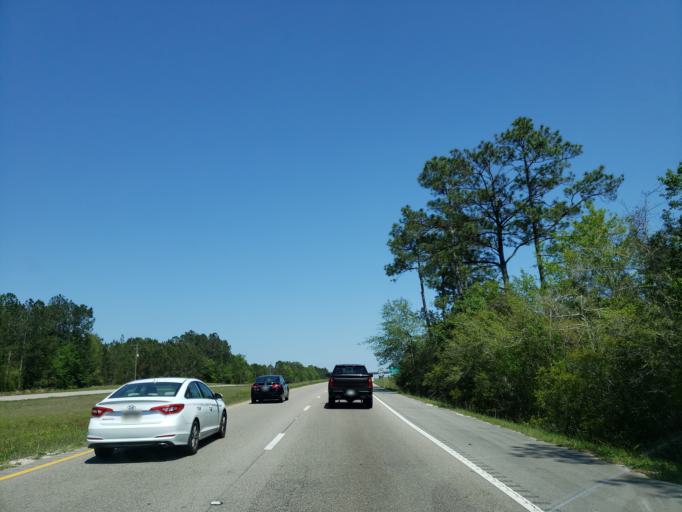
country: US
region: Mississippi
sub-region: Harrison County
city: Saucier
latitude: 30.6461
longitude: -89.1334
